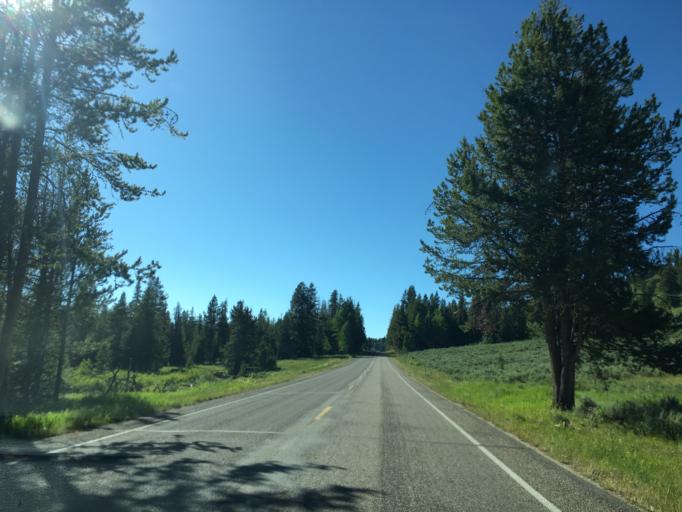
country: US
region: Wyoming
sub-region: Teton County
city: Jackson
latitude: 43.8599
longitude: -110.5309
